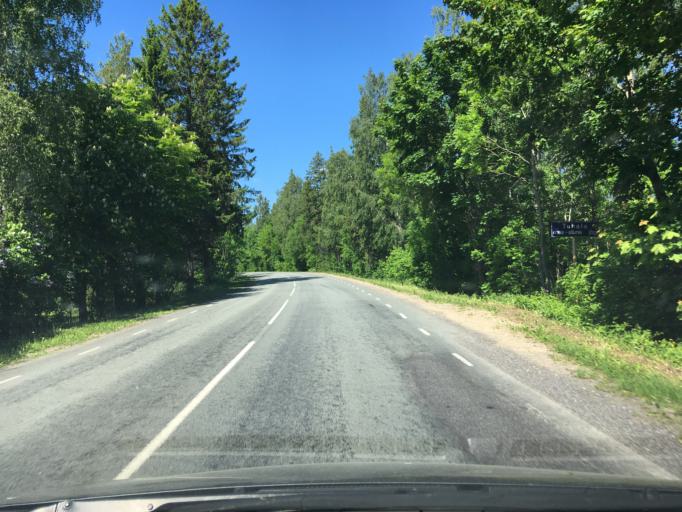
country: EE
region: Harju
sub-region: Rae vald
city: Vaida
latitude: 59.1979
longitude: 24.9684
